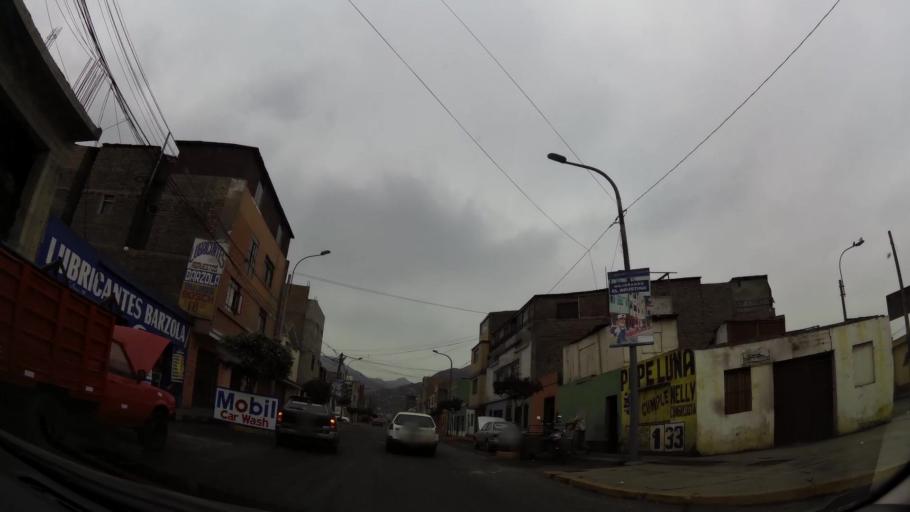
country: PE
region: Lima
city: Lima
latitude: -12.0519
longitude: -77.0089
